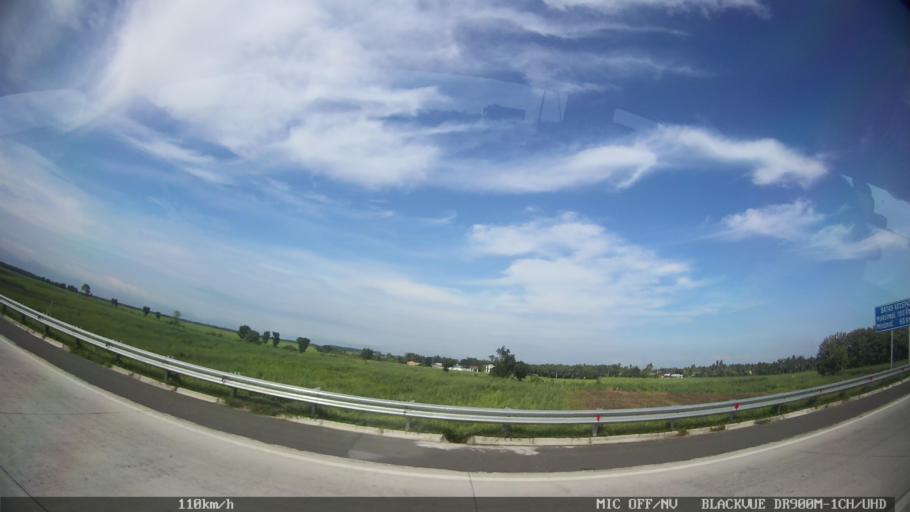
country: ID
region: North Sumatra
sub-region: Kabupaten Langkat
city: Stabat
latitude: 3.7005
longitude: 98.5397
